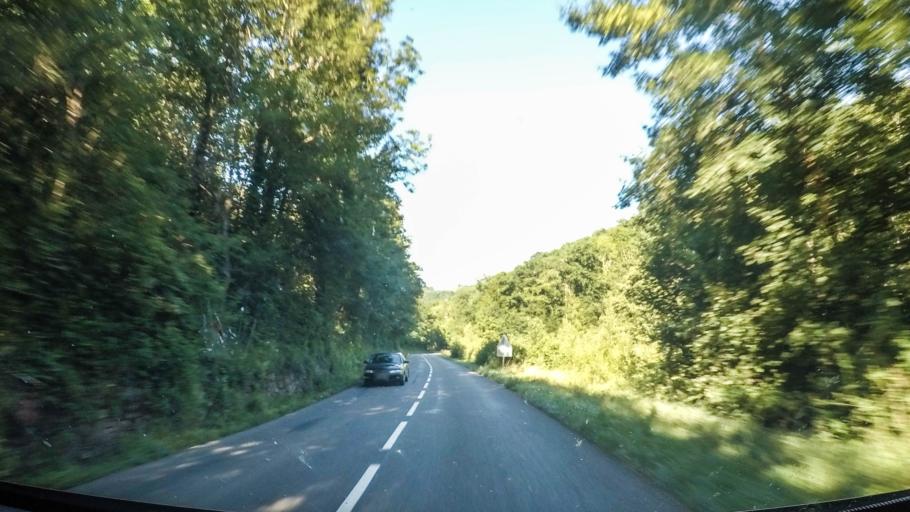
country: FR
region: Midi-Pyrenees
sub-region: Departement de l'Aveyron
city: Valady
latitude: 44.4663
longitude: 2.4395
